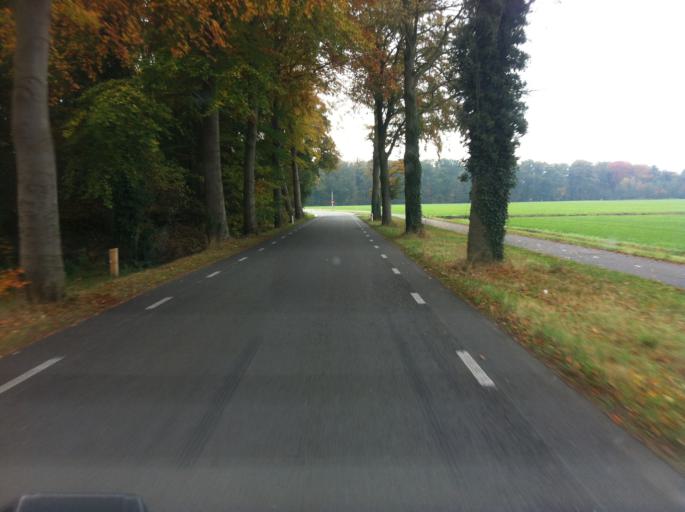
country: NL
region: Gelderland
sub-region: Gemeente Winterswijk
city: Winterswijk
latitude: 51.9820
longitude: 6.7565
